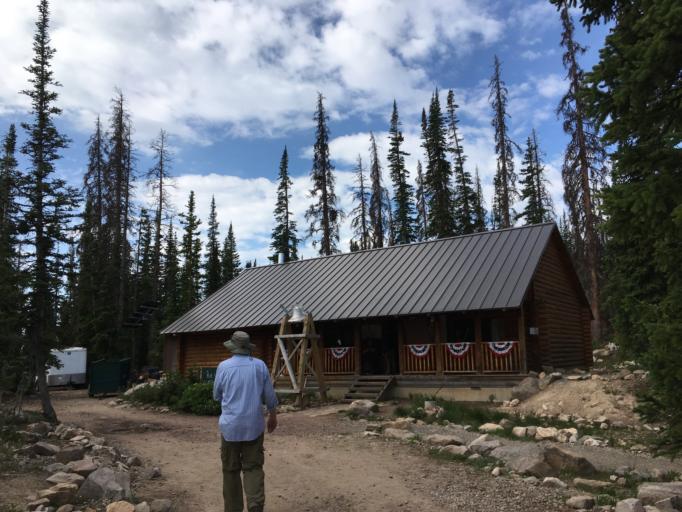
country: US
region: Utah
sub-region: Summit County
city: Kamas
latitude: 40.7193
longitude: -110.8849
